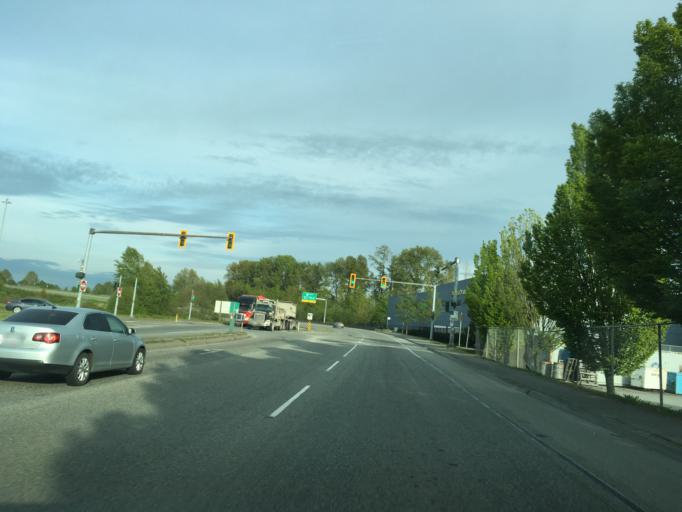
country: CA
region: British Columbia
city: Delta
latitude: 49.1683
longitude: -122.9766
